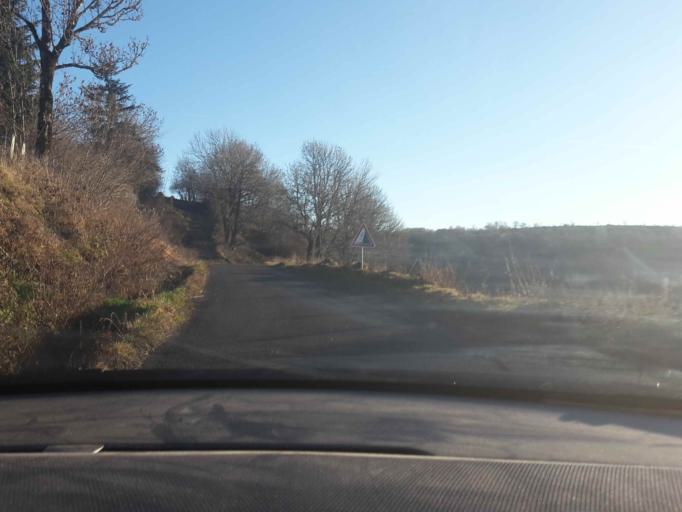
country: FR
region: Auvergne
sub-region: Departement du Cantal
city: Ydes
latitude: 45.2413
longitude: 2.5422
